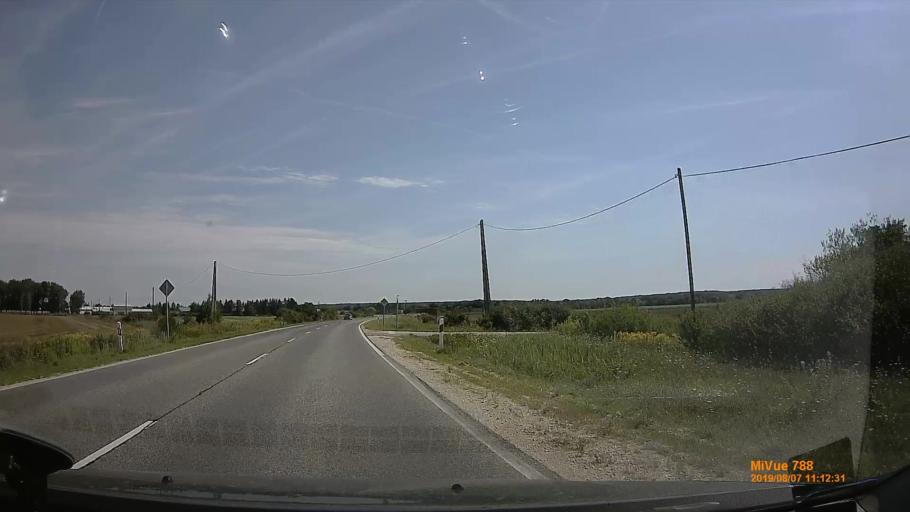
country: HU
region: Zala
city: Lenti
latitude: 46.6922
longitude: 16.5401
